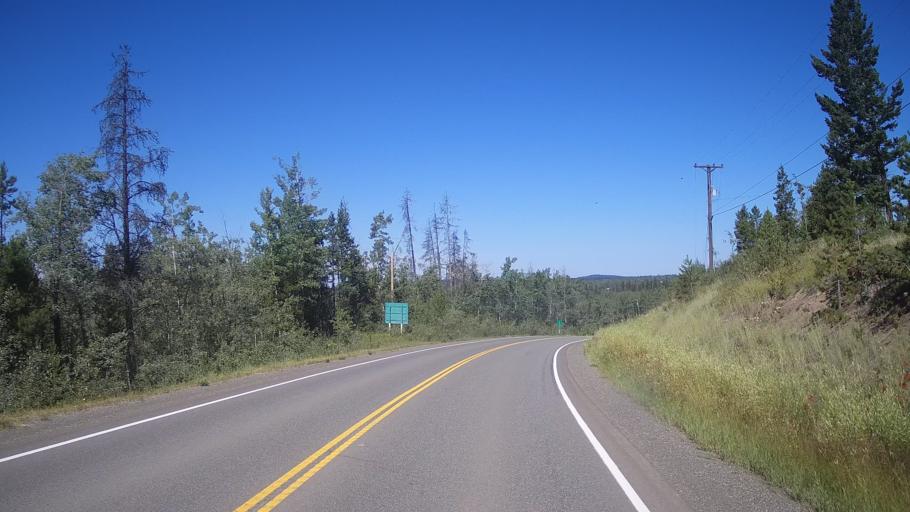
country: CA
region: British Columbia
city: Cache Creek
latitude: 51.5526
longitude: -121.1899
